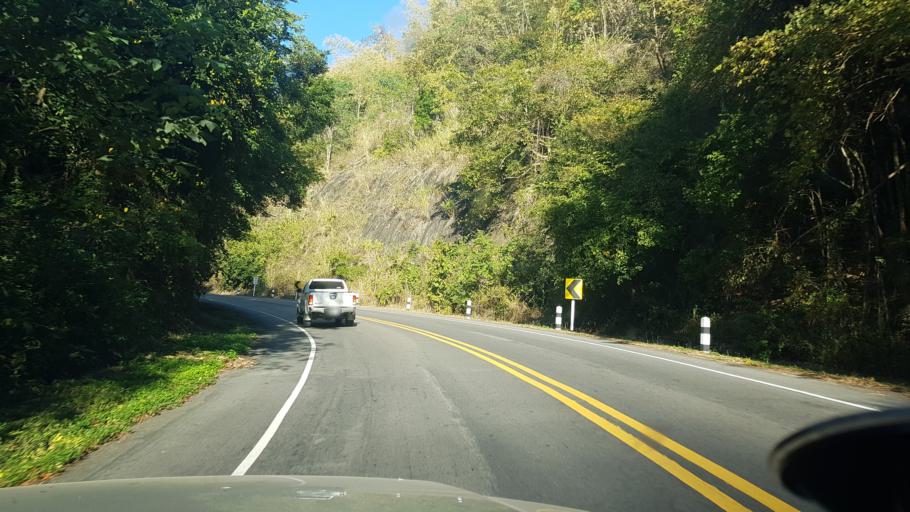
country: TH
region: Phetchabun
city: Nam Nao
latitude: 16.7595
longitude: 101.4886
